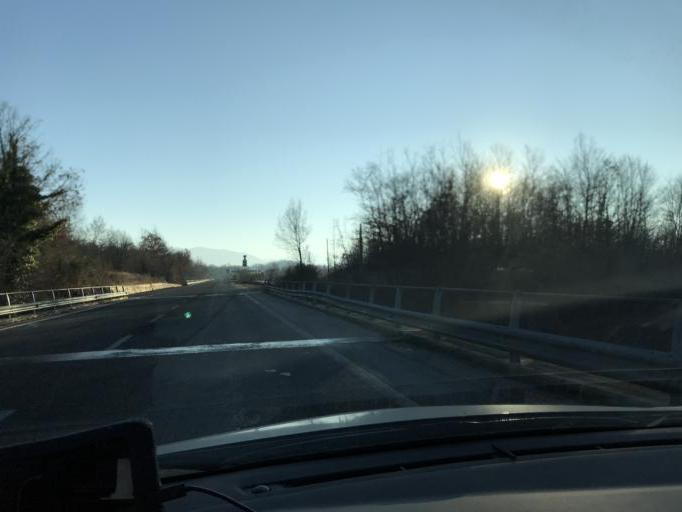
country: IT
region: Latium
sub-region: Provincia di Rieti
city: Fiamignano
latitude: 42.2621
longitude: 13.0879
